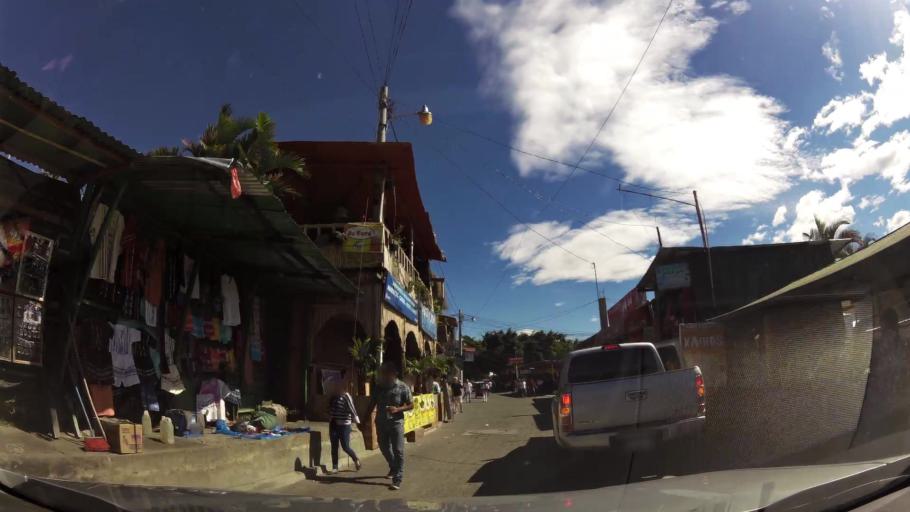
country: GT
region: Solola
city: Panajachel
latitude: 14.7365
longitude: -91.1593
